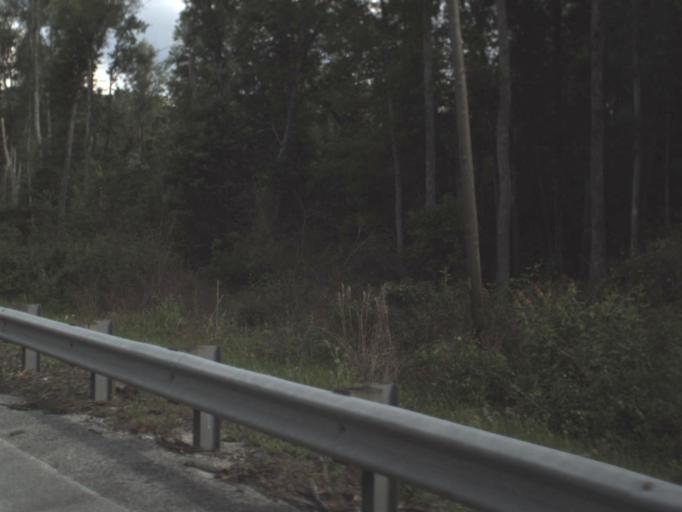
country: US
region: Florida
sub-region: Baker County
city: Macclenny
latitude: 30.5223
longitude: -82.2911
